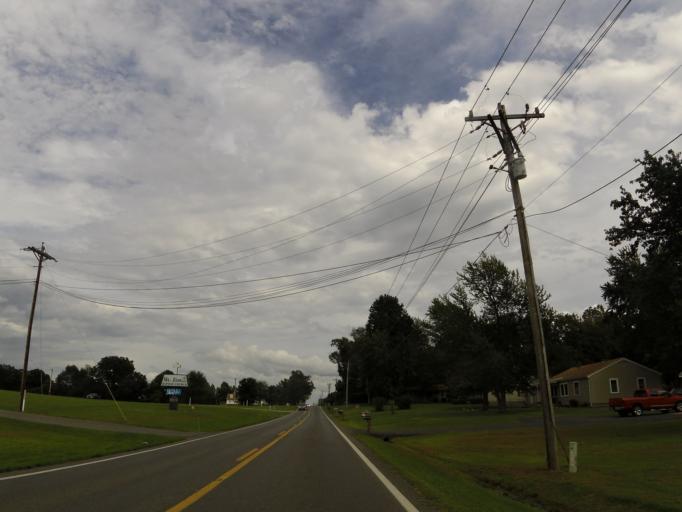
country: US
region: Kentucky
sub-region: McCracken County
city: Massac
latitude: 37.0219
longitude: -88.7796
